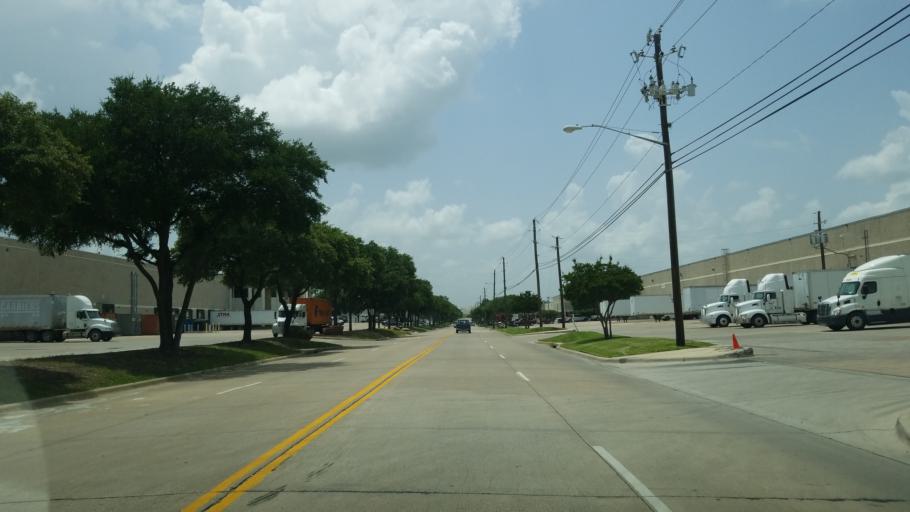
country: US
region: Texas
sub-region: Dallas County
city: Cockrell Hill
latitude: 32.7710
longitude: -96.8868
